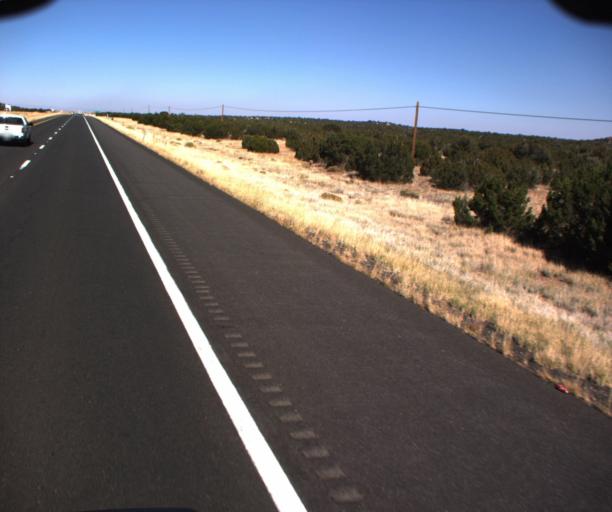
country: US
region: Arizona
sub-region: Coconino County
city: Flagstaff
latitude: 35.4771
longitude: -111.5569
